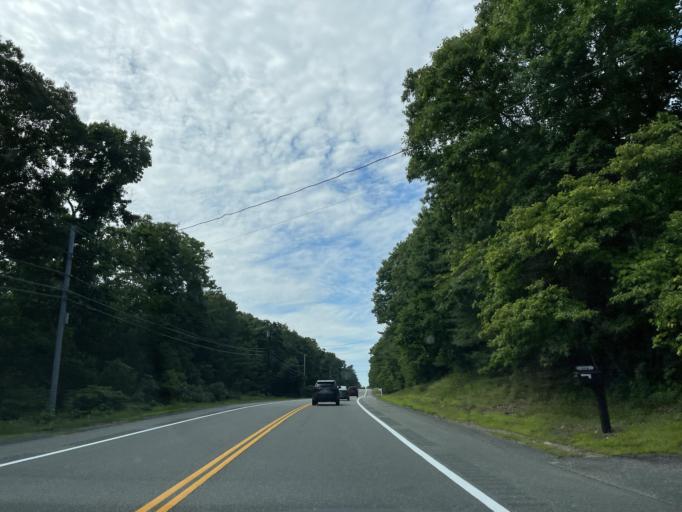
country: US
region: Rhode Island
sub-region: Kent County
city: West Greenwich
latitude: 41.6284
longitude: -71.6821
